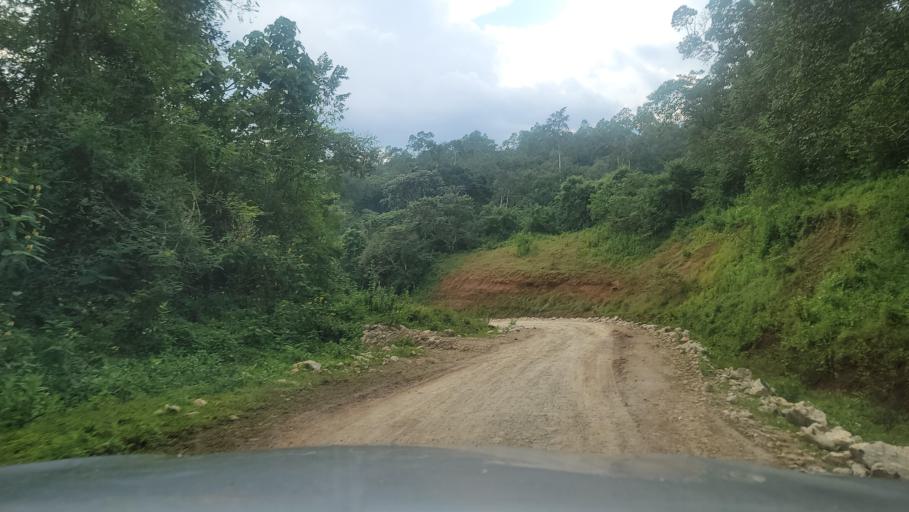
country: ET
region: Southern Nations, Nationalities, and People's Region
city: Bonga
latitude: 7.6178
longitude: 36.2086
